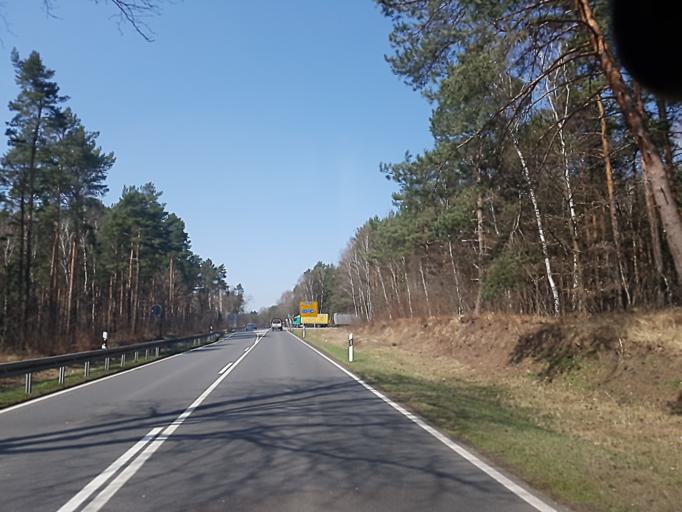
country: DE
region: Brandenburg
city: Tschernitz
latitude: 51.6291
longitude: 14.5763
